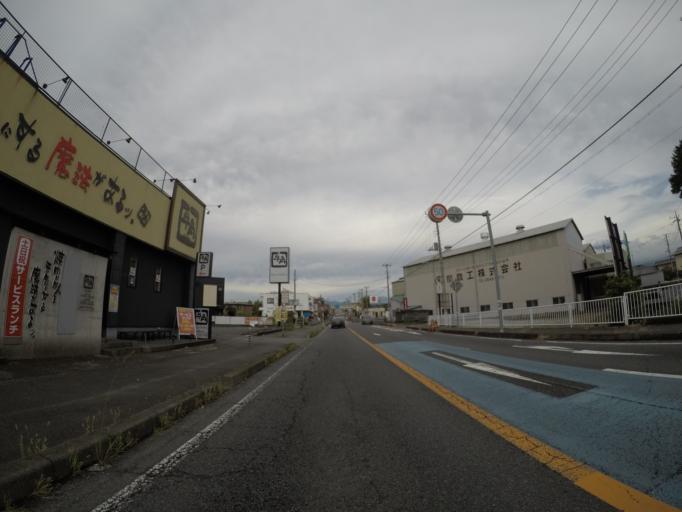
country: JP
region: Shizuoka
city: Fuji
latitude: 35.1885
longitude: 138.6526
